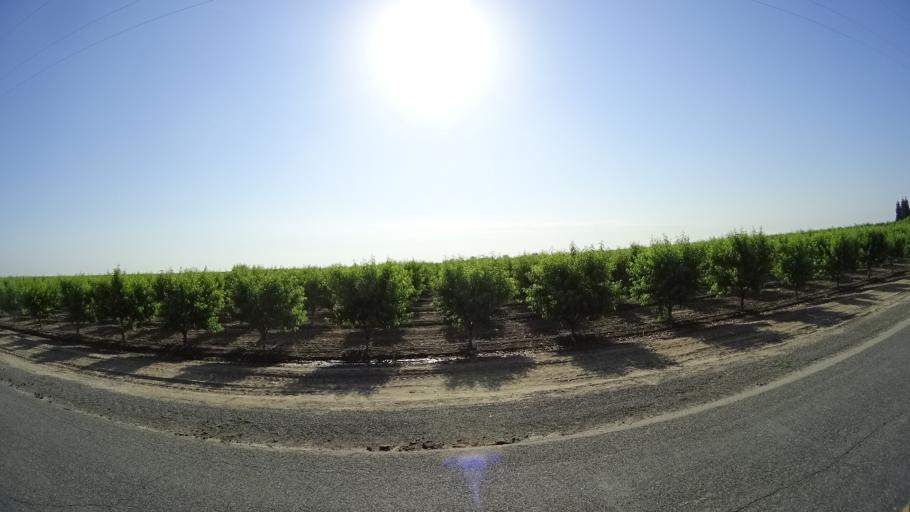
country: US
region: California
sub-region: Kings County
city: Home Garden
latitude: 36.2882
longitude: -119.5652
